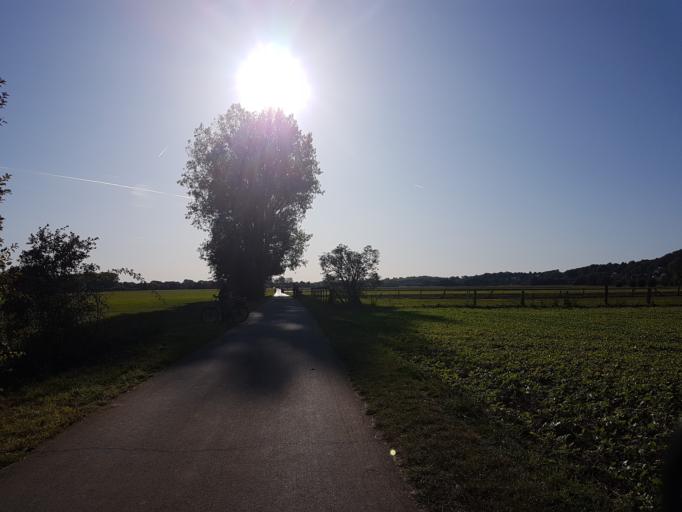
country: DE
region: North Rhine-Westphalia
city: Porta Westfalica
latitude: 52.2418
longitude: 8.8635
